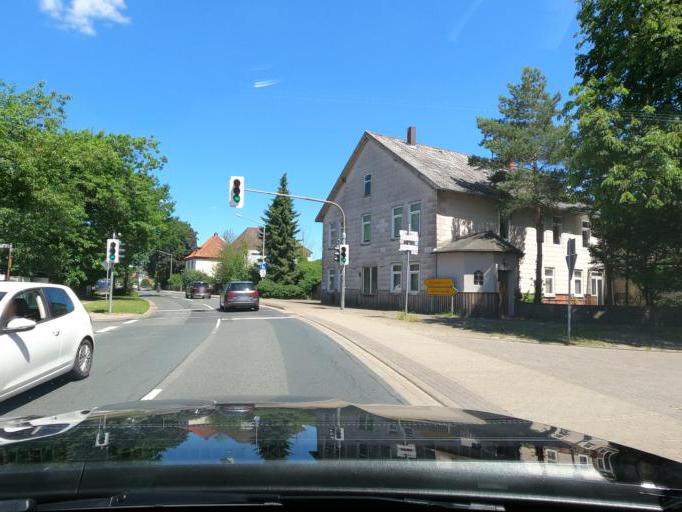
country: DE
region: Lower Saxony
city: Burgdorf
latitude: 52.4160
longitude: 9.9786
